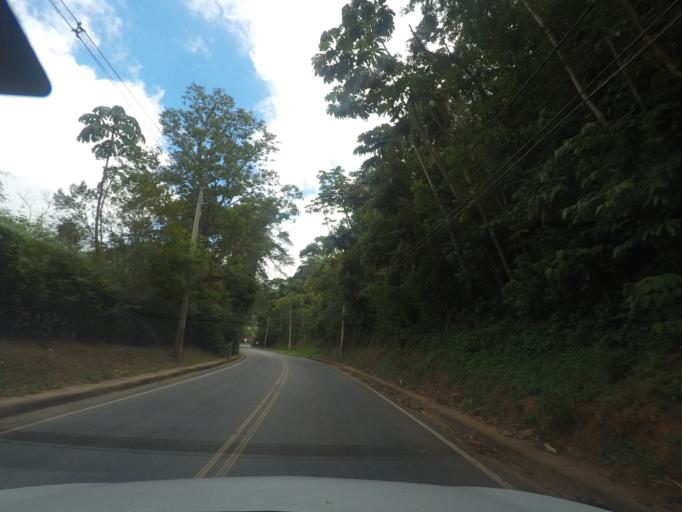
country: BR
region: Rio de Janeiro
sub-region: Teresopolis
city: Teresopolis
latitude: -22.3947
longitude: -42.9892
